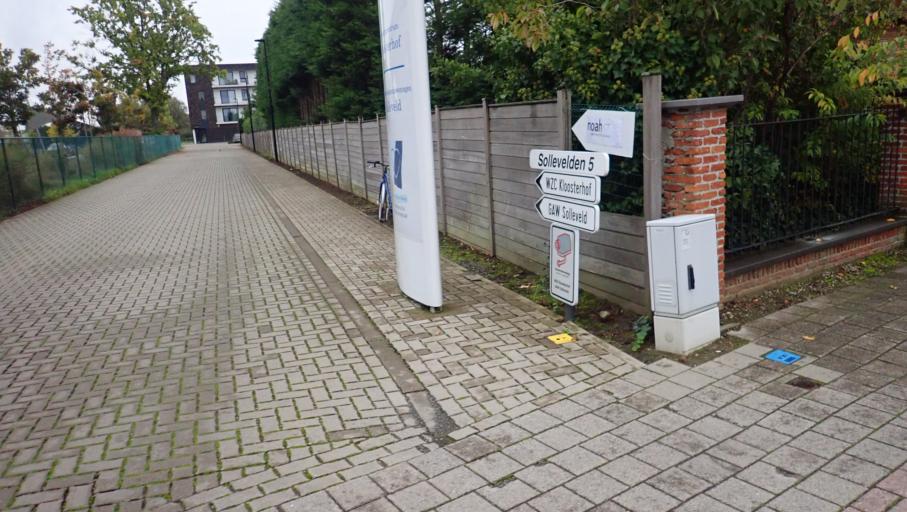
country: BE
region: Flanders
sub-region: Provincie Antwerpen
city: Berlaar
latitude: 51.1168
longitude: 4.6636
